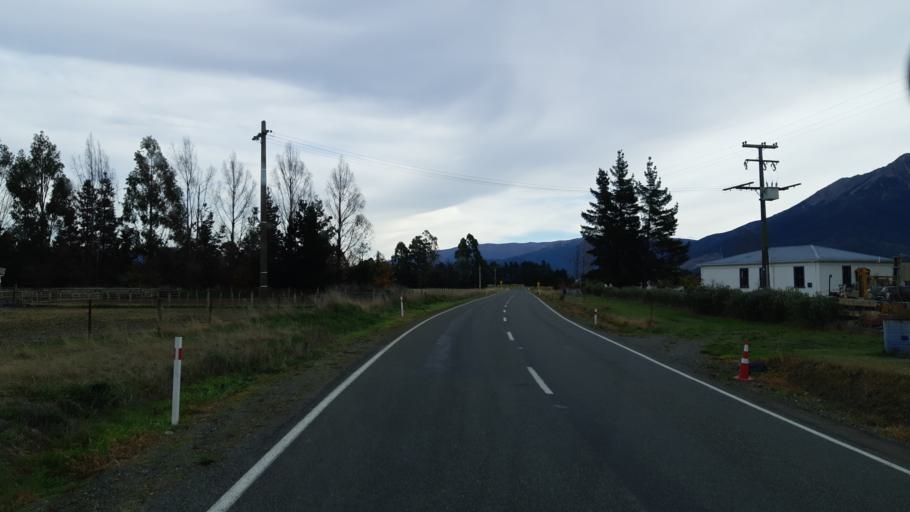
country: NZ
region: Tasman
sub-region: Tasman District
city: Brightwater
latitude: -41.6381
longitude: 173.3176
